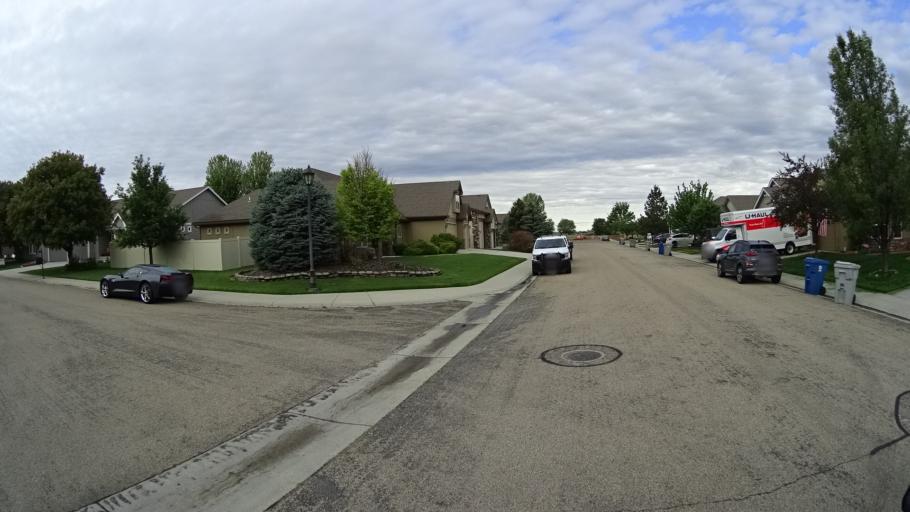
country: US
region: Idaho
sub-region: Ada County
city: Star
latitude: 43.6913
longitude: -116.5066
